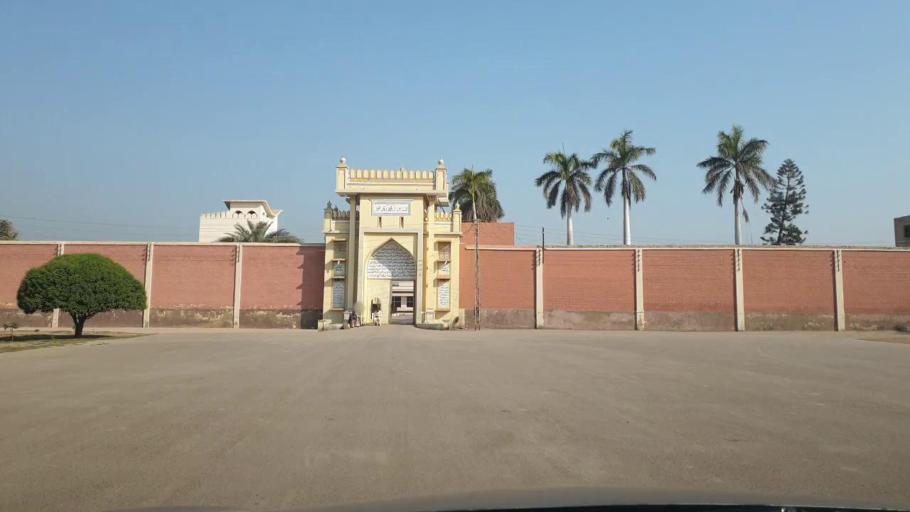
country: PK
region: Sindh
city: Tando Allahyar
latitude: 25.5111
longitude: 68.7208
